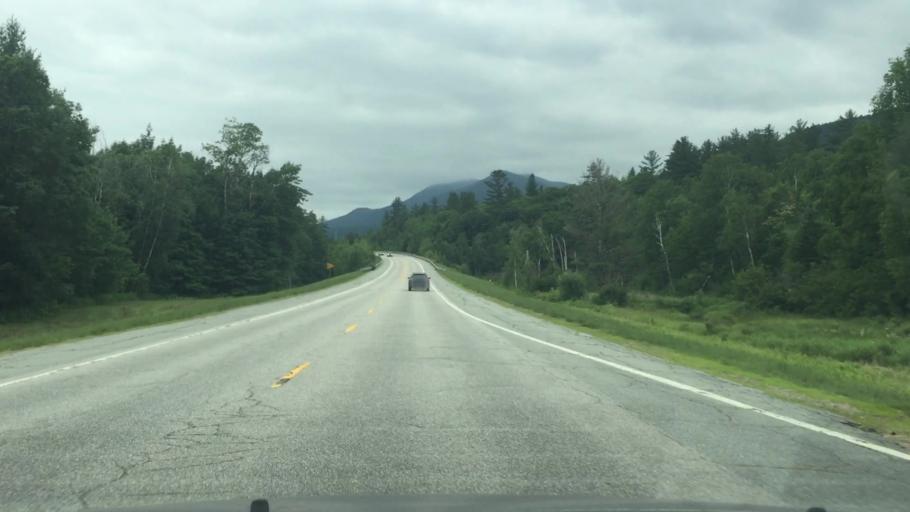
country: US
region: New Hampshire
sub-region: Carroll County
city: North Conway
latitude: 44.1169
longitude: -71.3542
